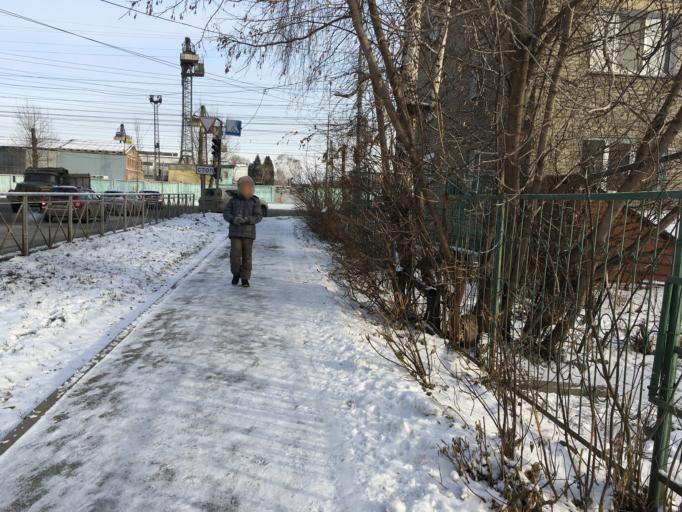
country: RU
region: Novosibirsk
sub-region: Novosibirskiy Rayon
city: Novosibirsk
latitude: 55.0590
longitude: 82.9753
